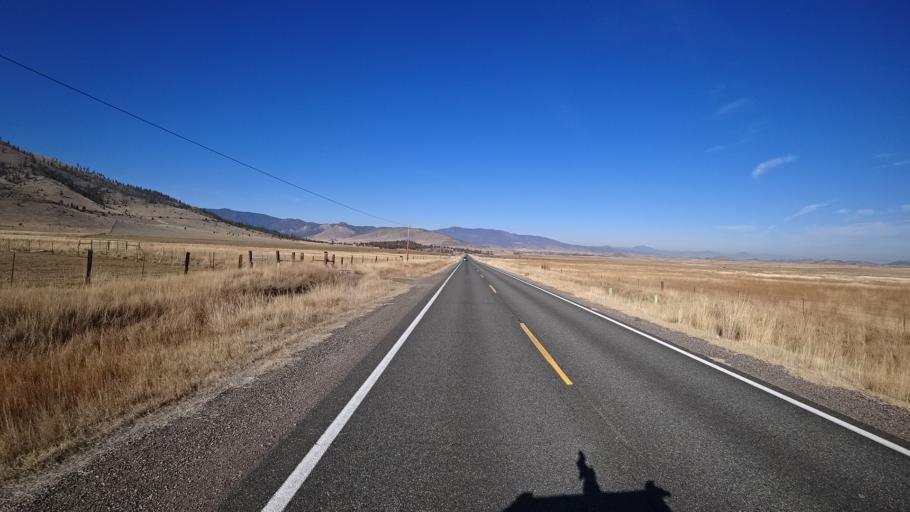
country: US
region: California
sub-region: Siskiyou County
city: Weed
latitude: 41.4835
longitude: -122.4979
